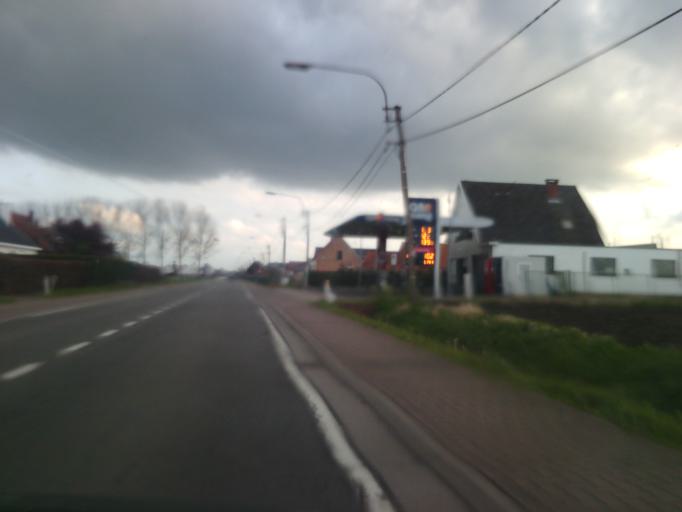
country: BE
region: Flanders
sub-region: Provincie Oost-Vlaanderen
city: Laarne
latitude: 51.0616
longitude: 3.8811
